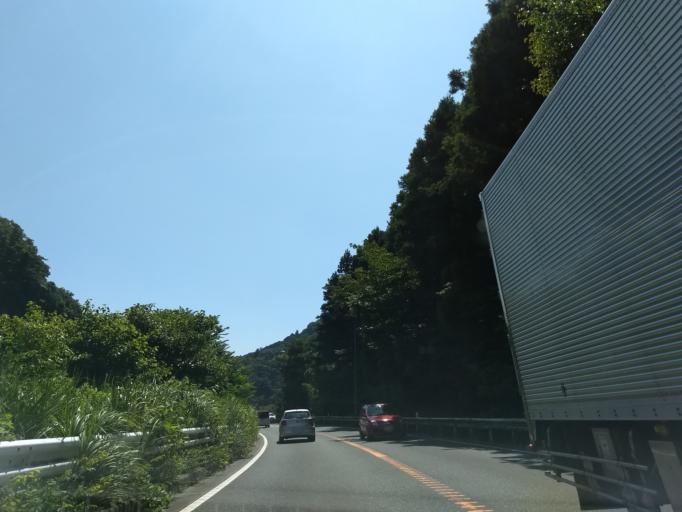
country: JP
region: Shizuoka
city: Gotemba
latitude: 35.3614
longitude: 139.0466
